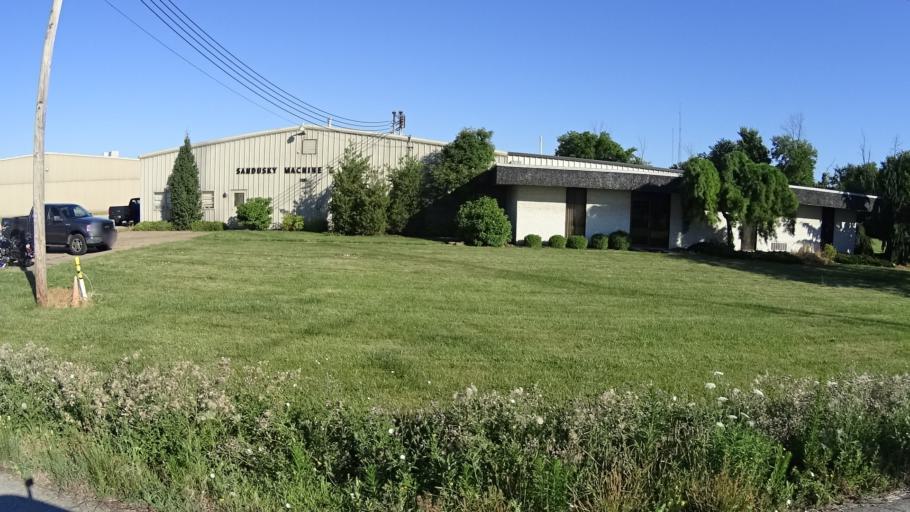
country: US
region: Ohio
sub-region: Erie County
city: Sandusky
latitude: 41.4343
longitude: -82.7408
